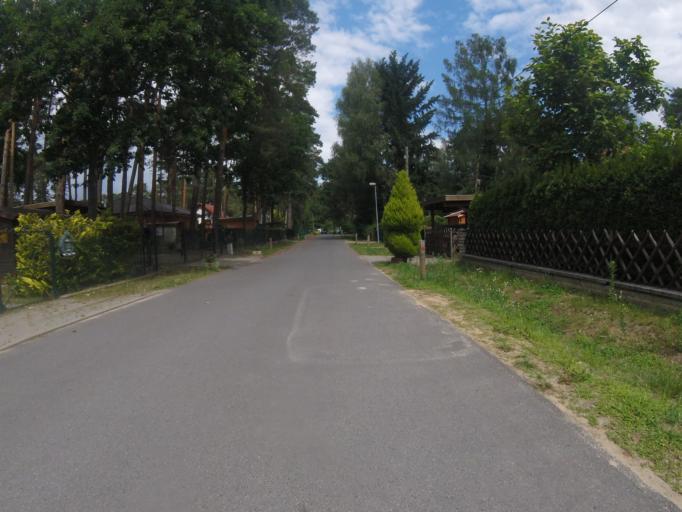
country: DE
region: Brandenburg
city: Bestensee
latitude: 52.2742
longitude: 13.6622
